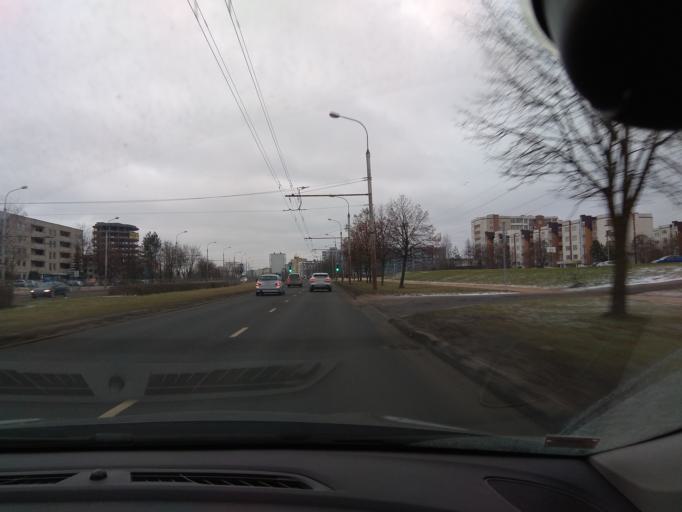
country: LT
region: Vilnius County
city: Justiniskes
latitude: 54.7182
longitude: 25.2321
